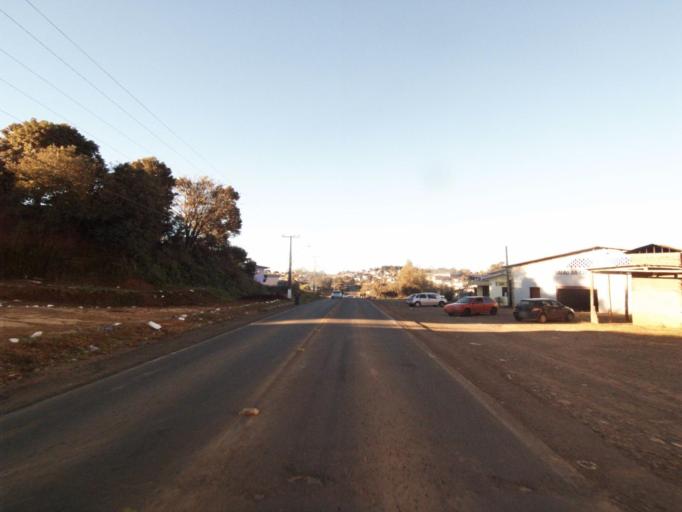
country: AR
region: Misiones
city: Bernardo de Irigoyen
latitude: -26.2641
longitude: -53.6236
